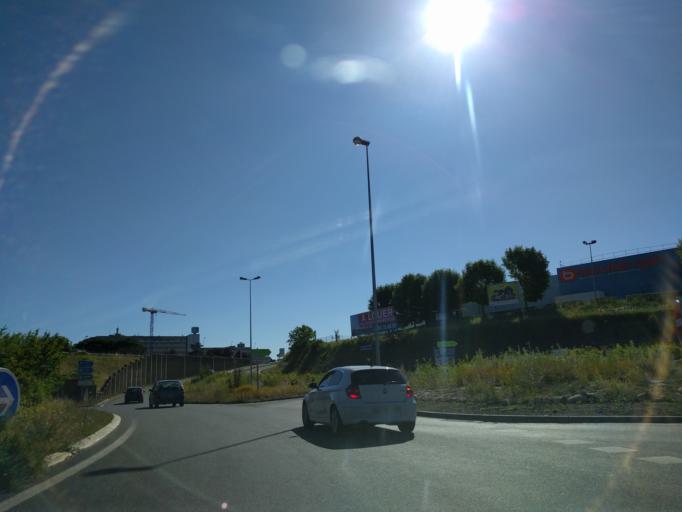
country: FR
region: Poitou-Charentes
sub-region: Departement des Deux-Sevres
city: Chauray
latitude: 46.3388
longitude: -0.4084
